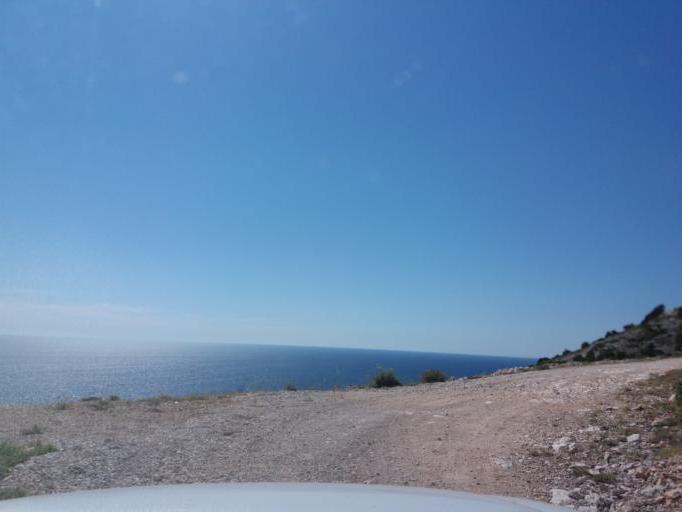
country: HR
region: Zadarska
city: Ugljan
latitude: 44.0084
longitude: 15.0346
